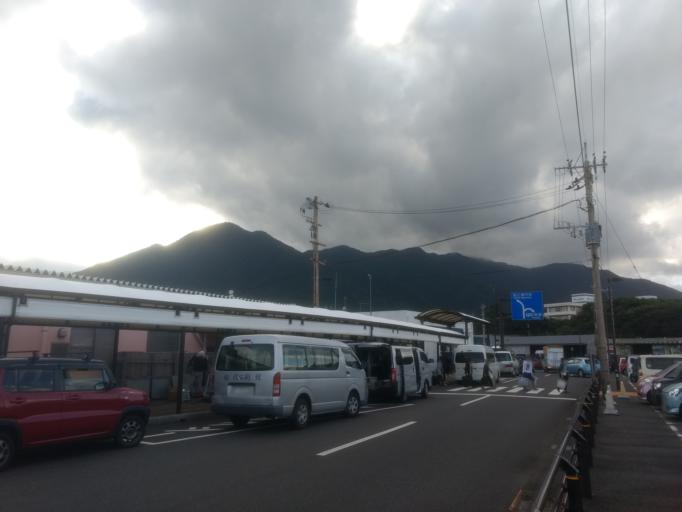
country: JP
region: Kagoshima
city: Nishinoomote
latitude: 30.4326
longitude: 130.5713
